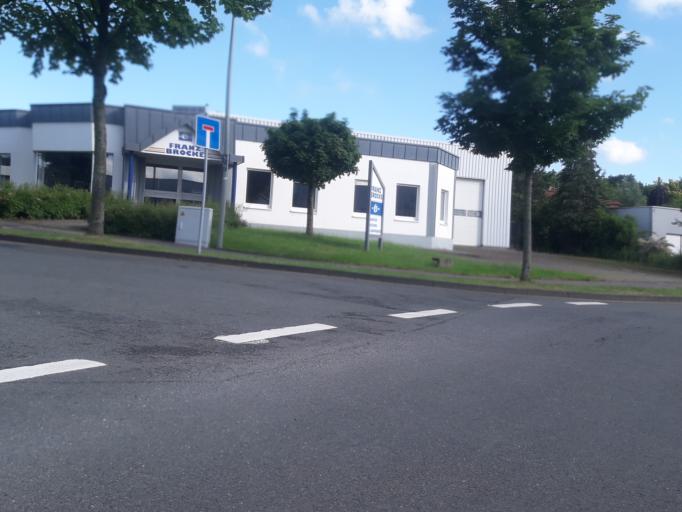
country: DE
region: North Rhine-Westphalia
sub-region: Regierungsbezirk Detmold
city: Paderborn
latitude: 51.7285
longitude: 8.7948
